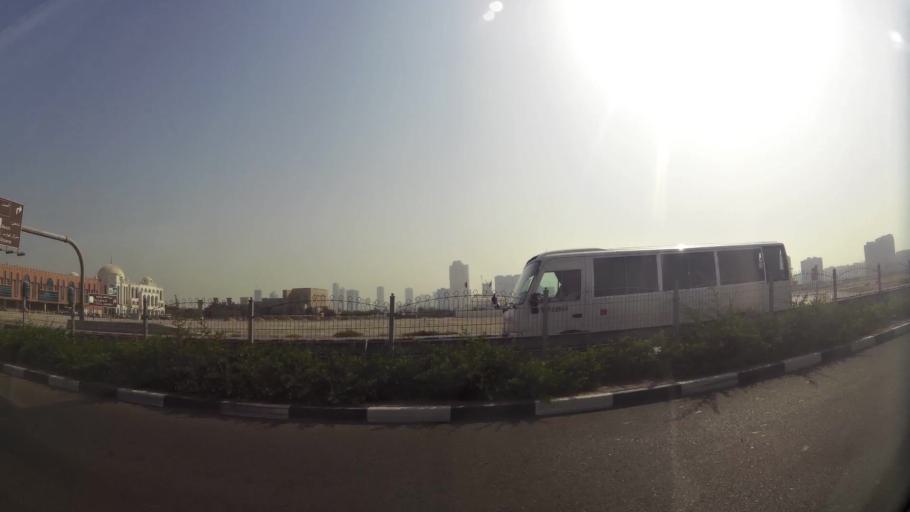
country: AE
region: Ash Shariqah
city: Sharjah
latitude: 25.2928
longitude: 55.3516
